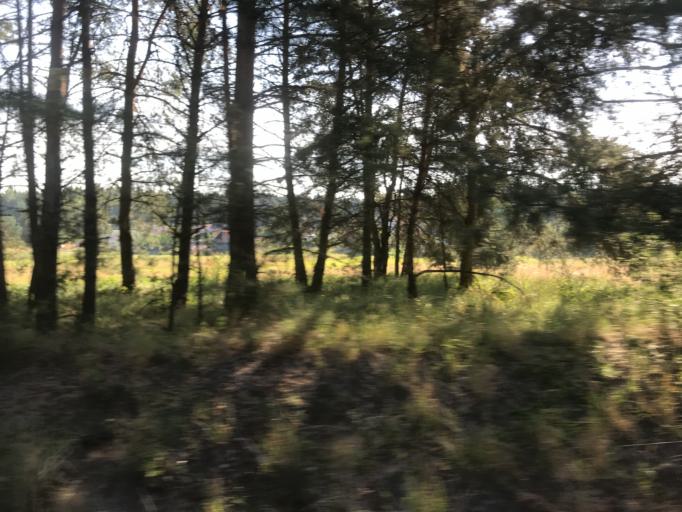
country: CZ
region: Jihocesky
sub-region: Okres Tabor
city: Veseli nad Luznici
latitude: 49.1548
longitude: 14.7247
